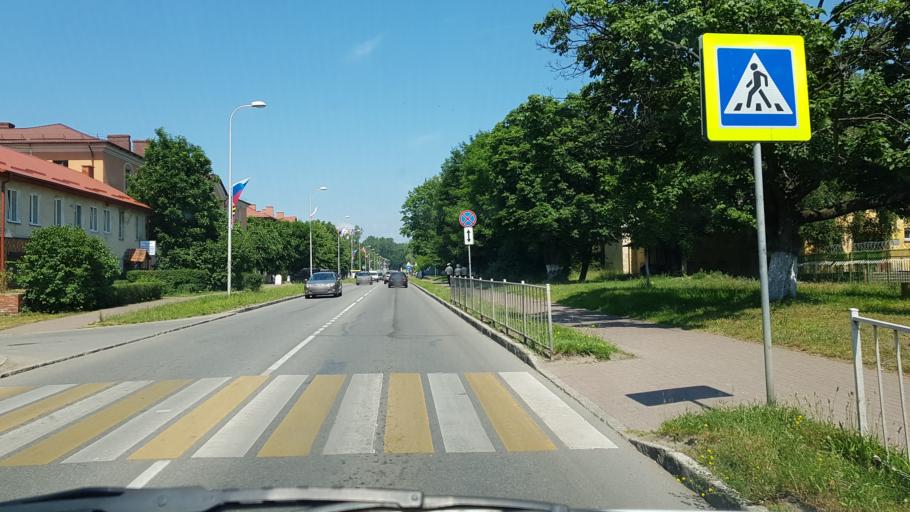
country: RU
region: Kaliningrad
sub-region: Gorod Kaliningrad
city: Baltiysk
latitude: 54.6572
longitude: 19.9131
